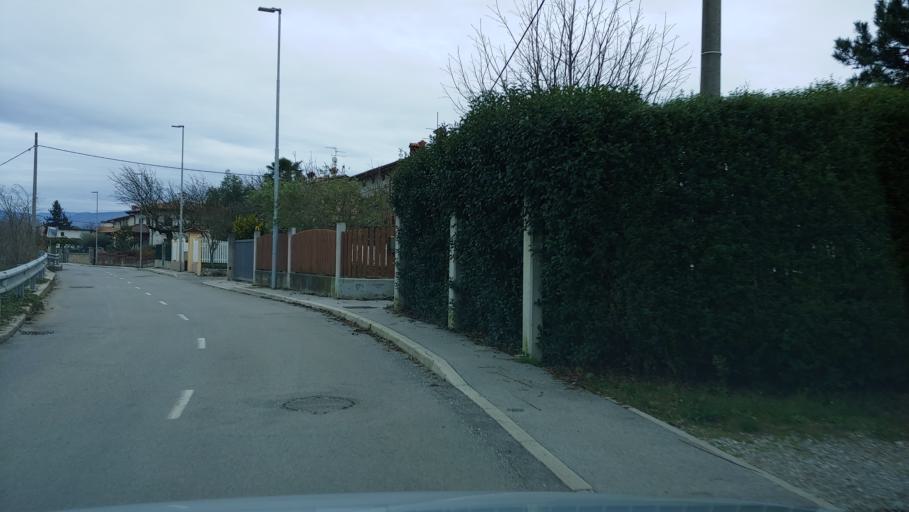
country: SI
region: Miren-Kostanjevica
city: Miren
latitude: 45.8935
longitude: 13.6155
